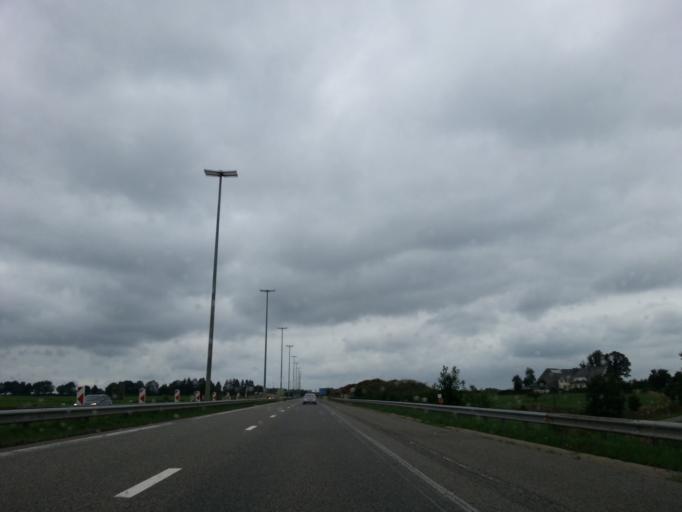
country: BE
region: Wallonia
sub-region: Province de Liege
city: Saint-Vith
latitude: 50.2751
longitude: 6.1099
